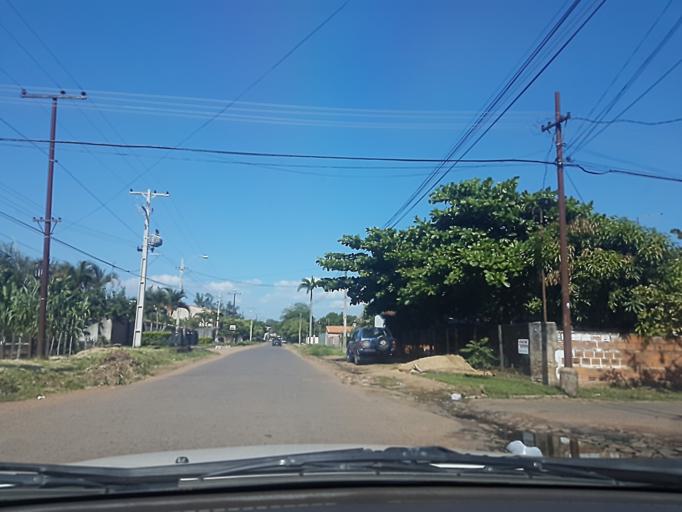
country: PY
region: Central
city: Limpio
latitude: -25.1744
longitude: -57.4769
